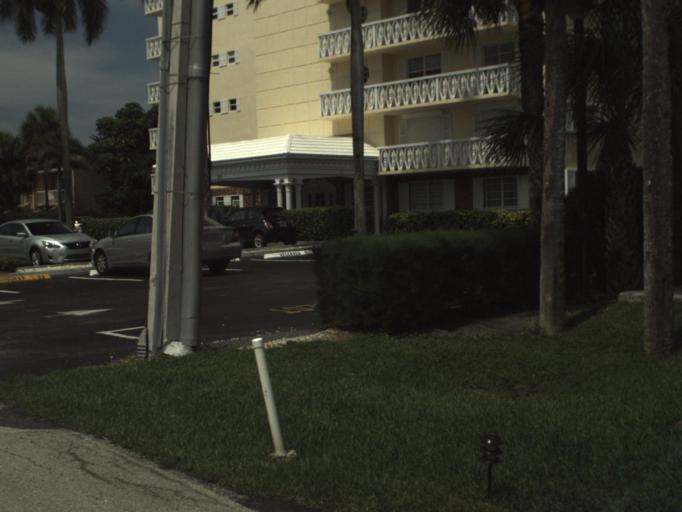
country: US
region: Florida
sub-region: Broward County
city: Hillsboro Beach
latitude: 26.2954
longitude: -80.0788
